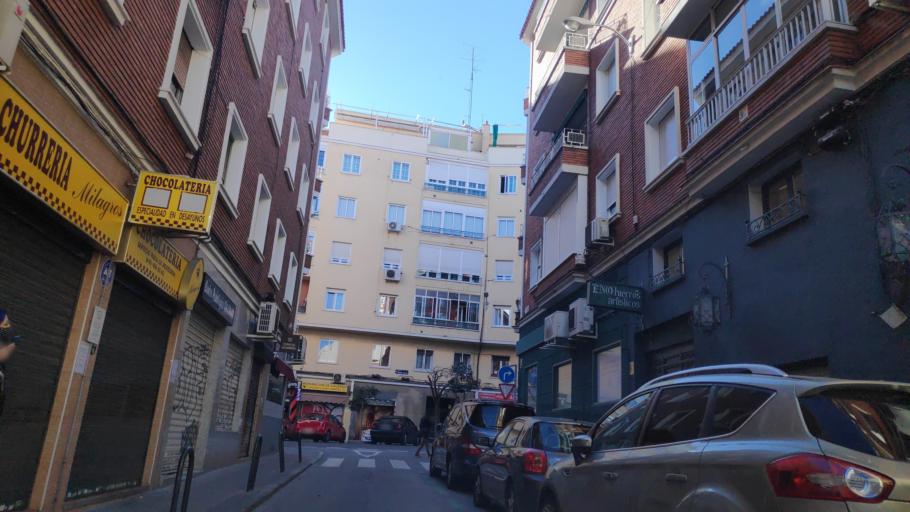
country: ES
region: Madrid
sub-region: Provincia de Madrid
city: Chamartin
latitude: 40.4479
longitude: -3.6752
